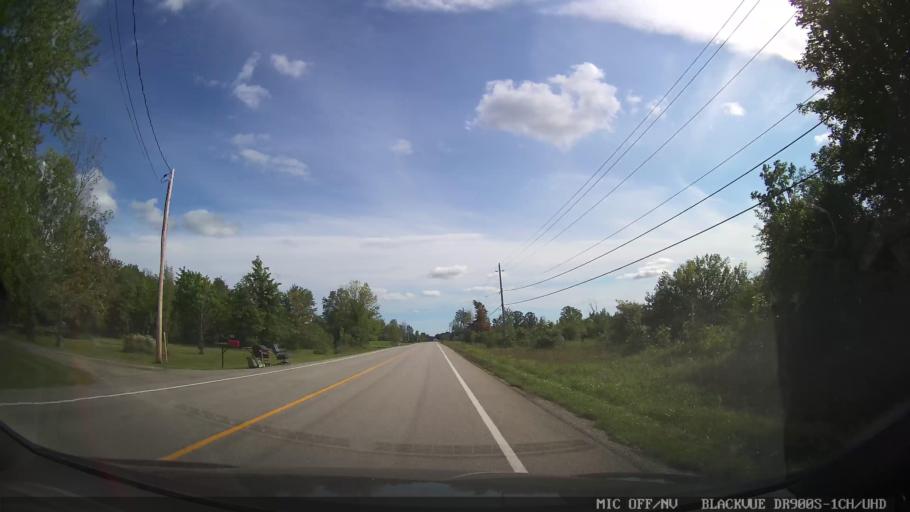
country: CA
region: Ontario
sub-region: Lanark County
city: Smiths Falls
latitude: 44.9343
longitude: -75.9618
